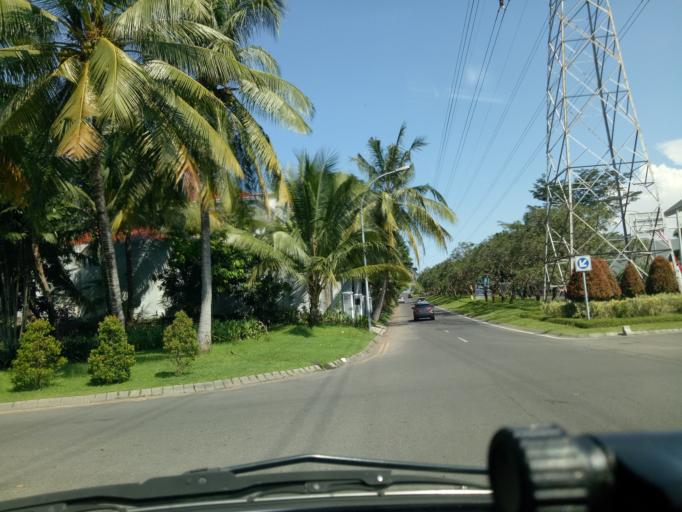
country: ID
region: East Java
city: Driyorejo
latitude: -7.2884
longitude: 112.6479
